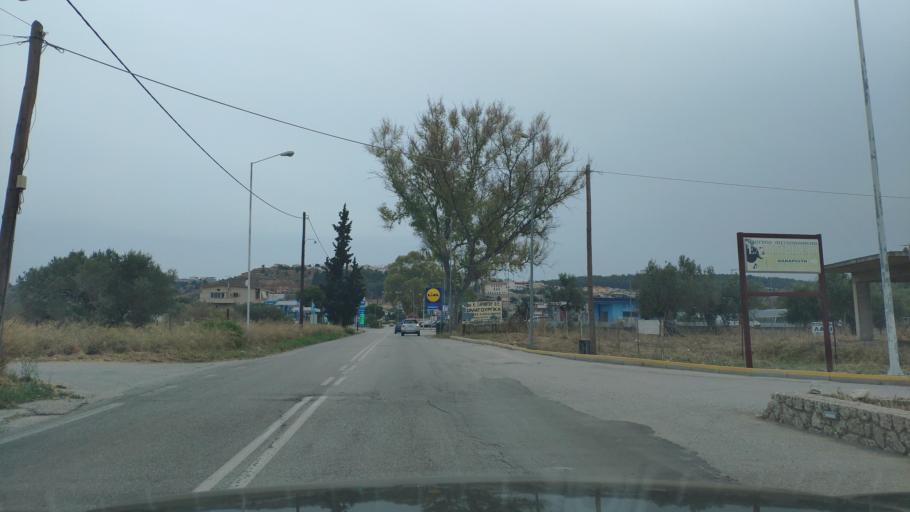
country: GR
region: Peloponnese
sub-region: Nomos Argolidos
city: Kranidi
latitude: 37.3909
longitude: 23.1577
